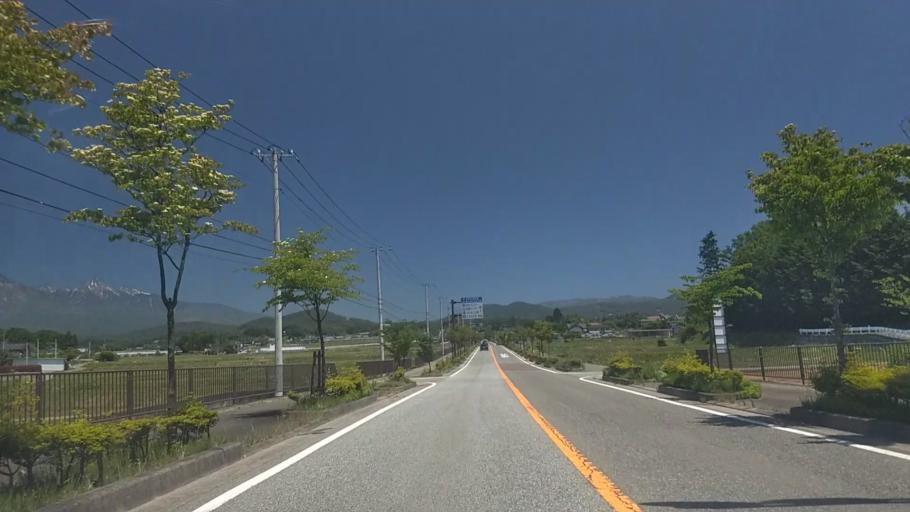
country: JP
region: Yamanashi
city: Nirasaki
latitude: 35.8244
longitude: 138.4287
